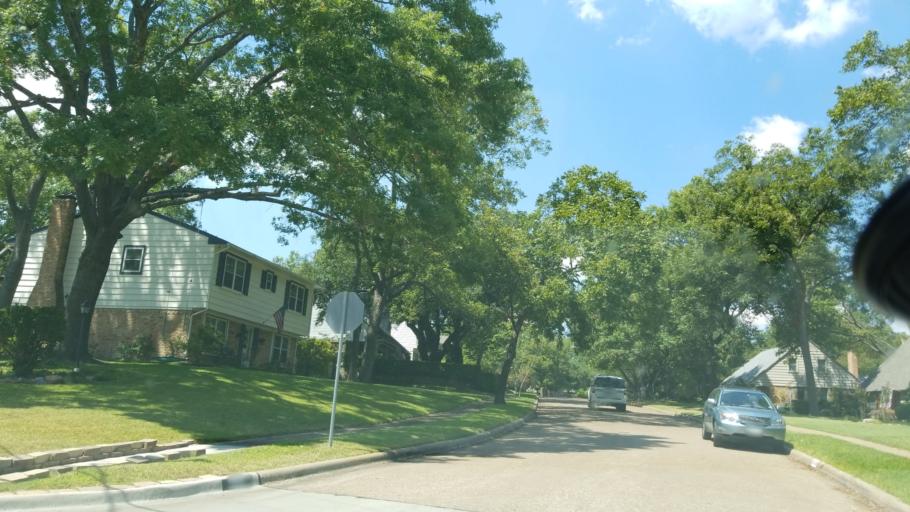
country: US
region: Texas
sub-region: Dallas County
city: Richardson
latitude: 32.8831
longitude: -96.7131
